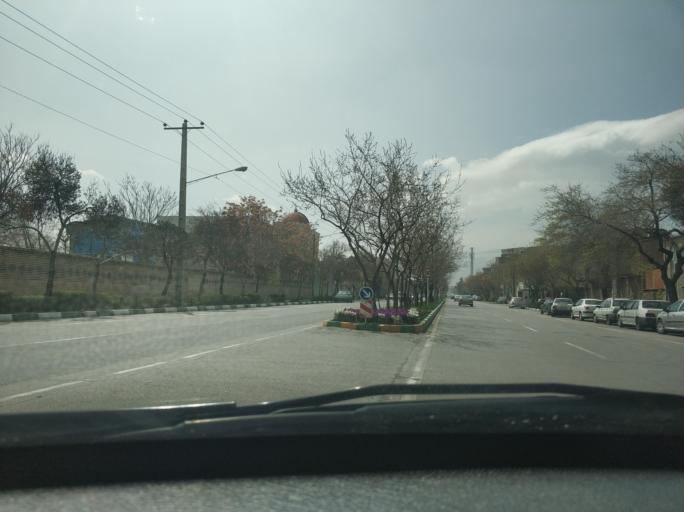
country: IR
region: Razavi Khorasan
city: Mashhad
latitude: 36.2792
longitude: 59.5770
